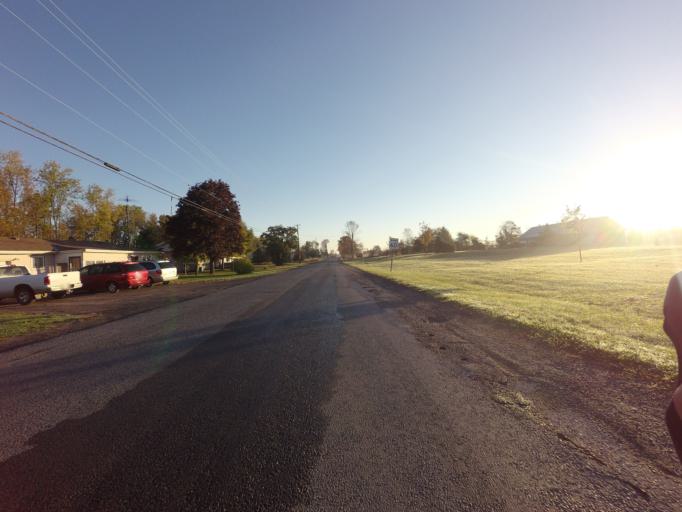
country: CA
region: Ontario
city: Quinte West
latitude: 44.0287
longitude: -77.5633
